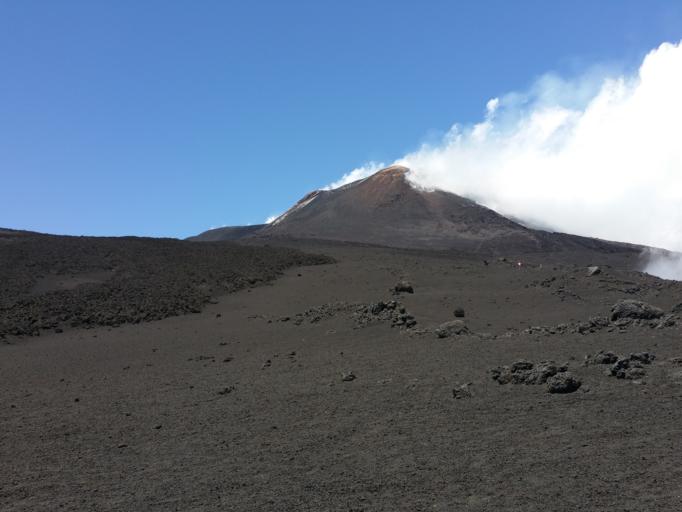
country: IT
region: Sicily
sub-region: Catania
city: Milo
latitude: 37.7326
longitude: 15.0093
